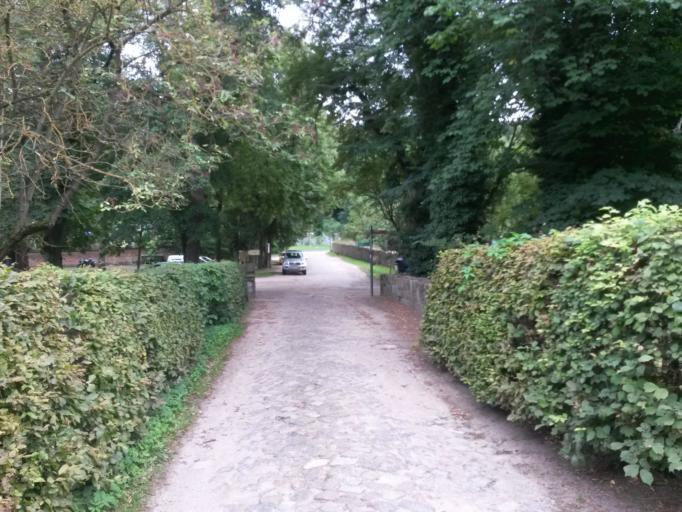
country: DE
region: Brandenburg
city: Chorin
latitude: 52.8930
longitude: 13.8850
